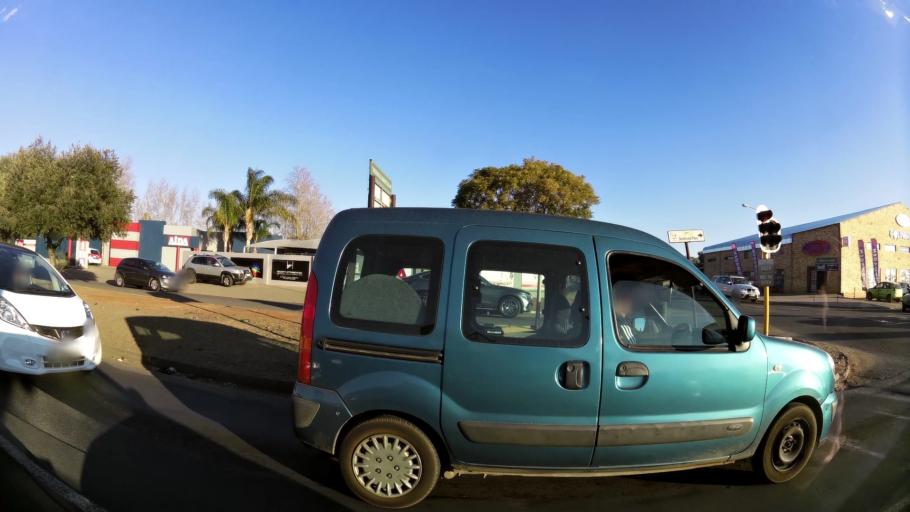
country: ZA
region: Northern Cape
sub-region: Frances Baard District Municipality
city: Kimberley
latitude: -28.7442
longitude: 24.7550
